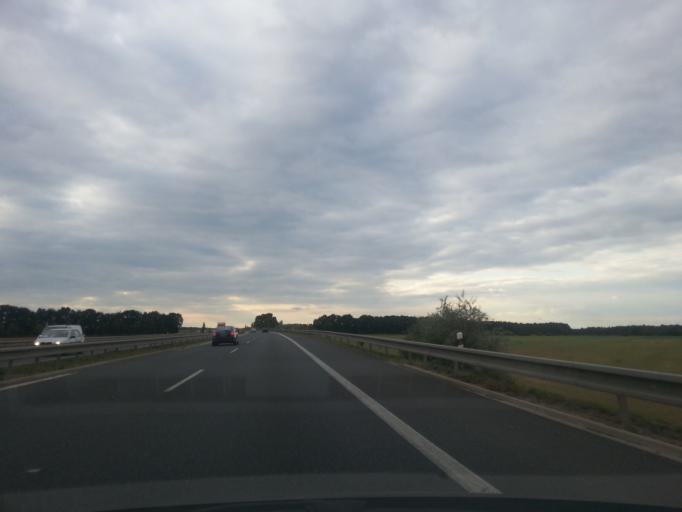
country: CZ
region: Central Bohemia
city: Jenec
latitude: 50.0967
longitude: 14.1875
